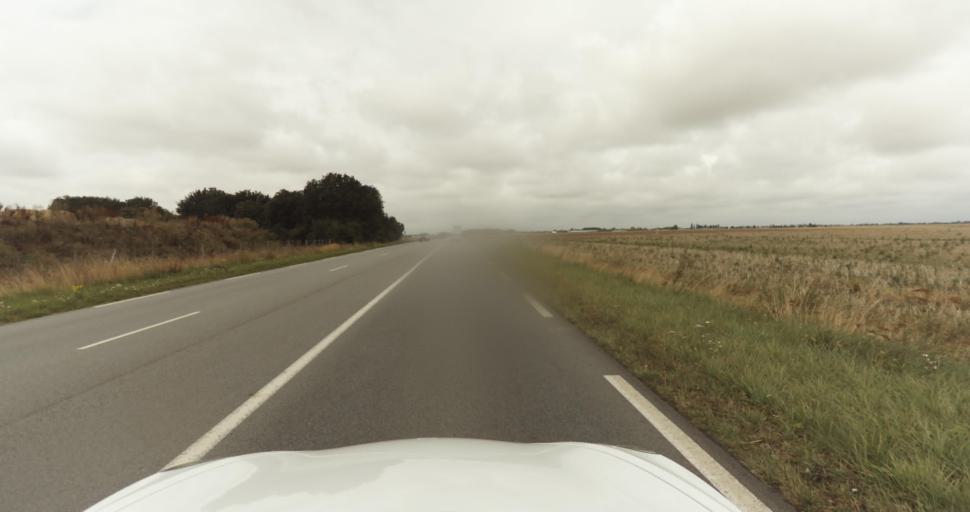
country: FR
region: Haute-Normandie
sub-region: Departement de l'Eure
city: Claville
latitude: 49.0536
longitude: 1.0541
